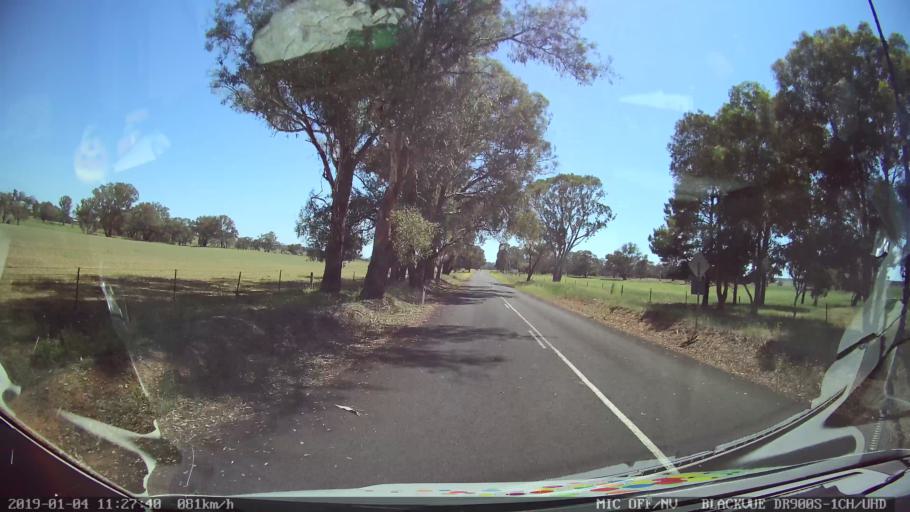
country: AU
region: New South Wales
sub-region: Cabonne
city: Molong
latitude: -33.1072
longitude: 148.7651
